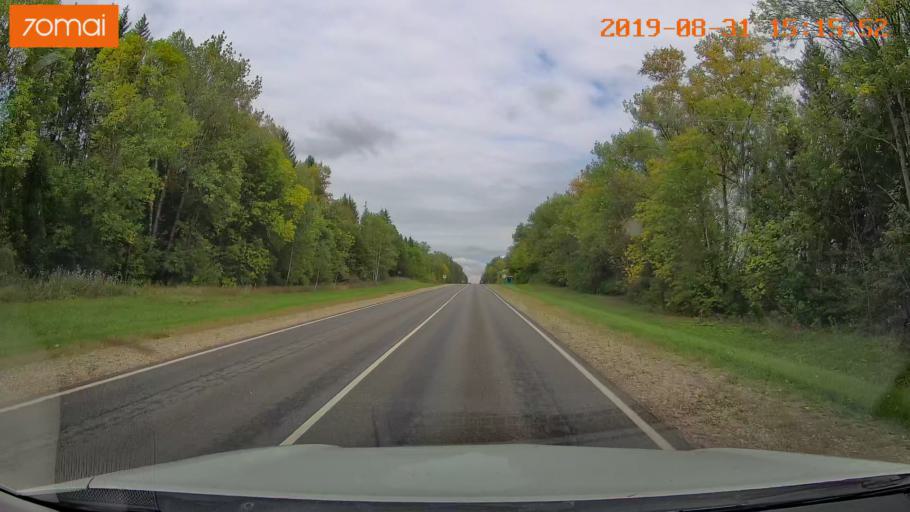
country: RU
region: Kaluga
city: Baryatino
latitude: 54.4551
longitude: 34.3367
